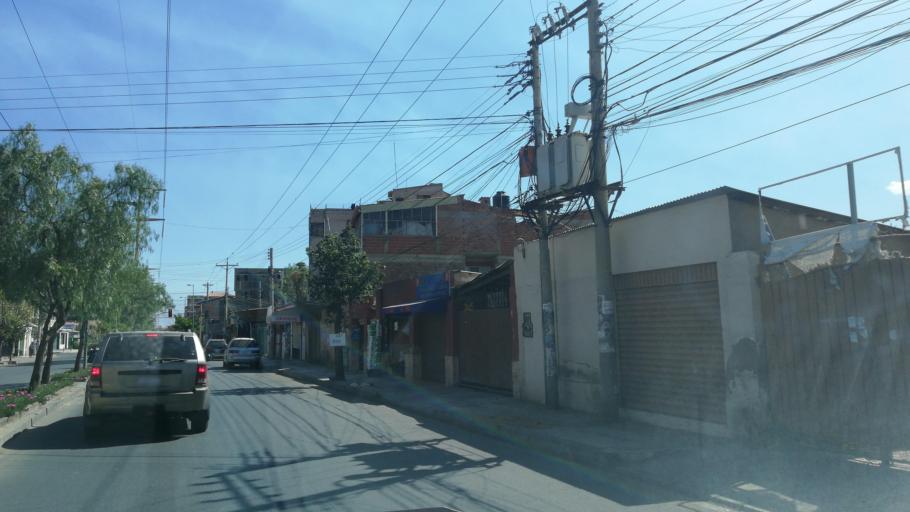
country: BO
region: Cochabamba
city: Cochabamba
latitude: -17.3960
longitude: -66.1769
